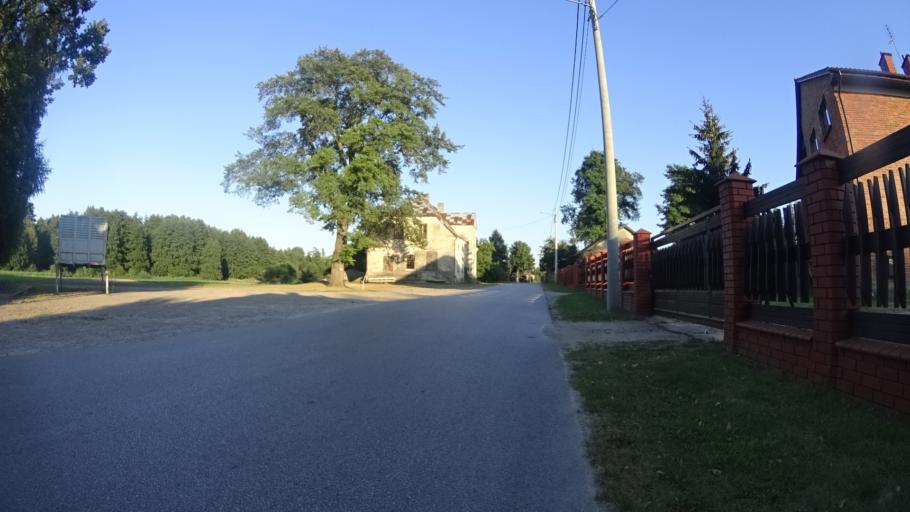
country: PL
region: Masovian Voivodeship
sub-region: Powiat grojecki
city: Goszczyn
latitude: 51.6974
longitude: 20.8104
